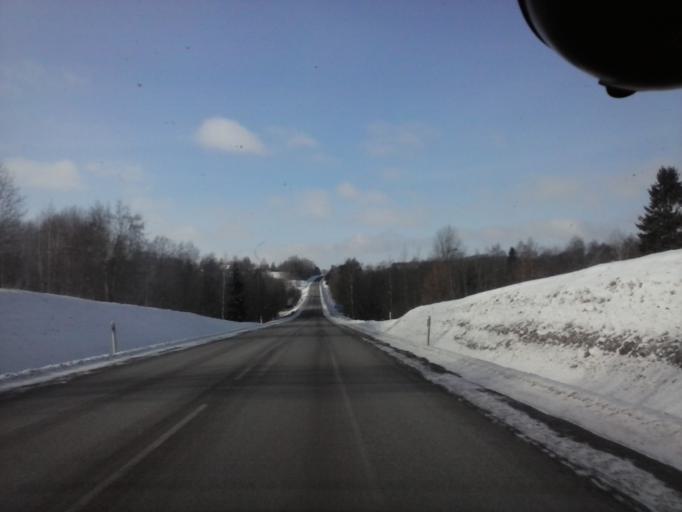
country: EE
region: Tartu
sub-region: Puhja vald
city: Puhja
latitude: 58.3440
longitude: 26.3735
